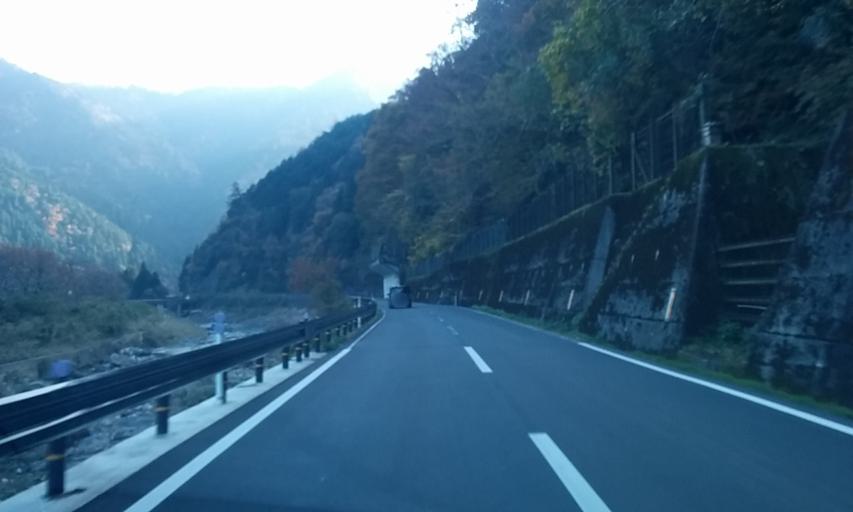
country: JP
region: Fukui
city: Obama
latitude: 35.3015
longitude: 135.6144
